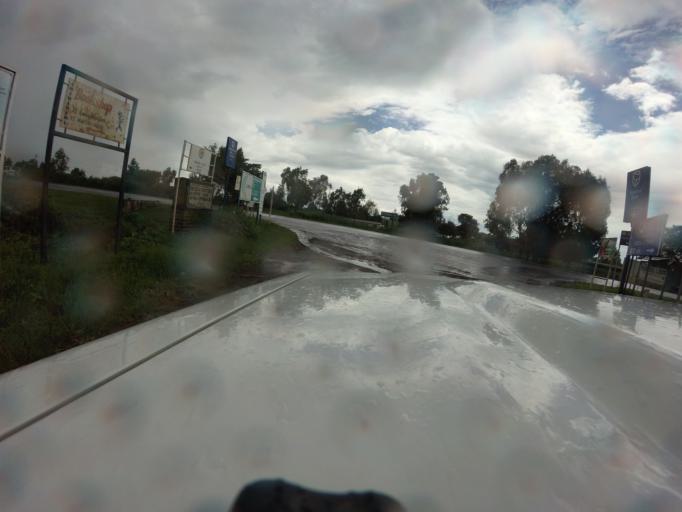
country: MW
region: Central Region
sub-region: Dedza District
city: Dedza
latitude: -14.3832
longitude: 34.3063
